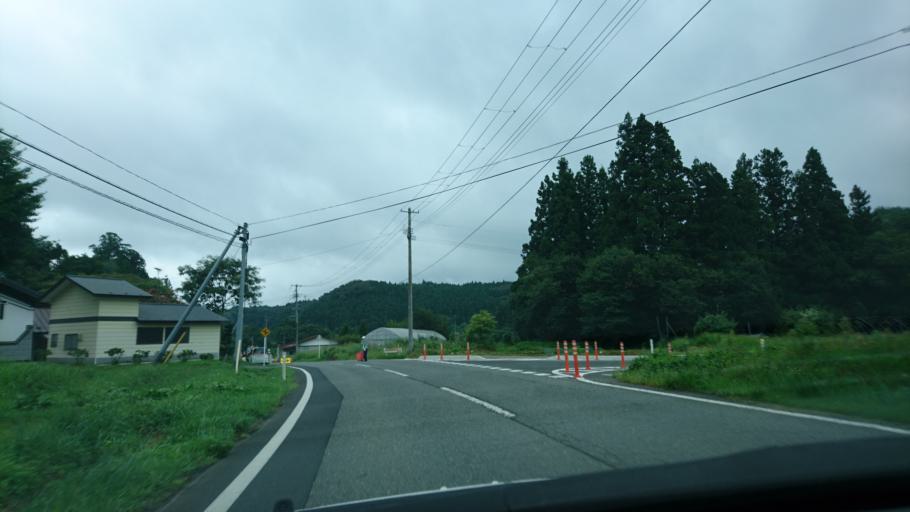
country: JP
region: Iwate
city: Ichinoseki
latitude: 38.9095
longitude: 141.0618
